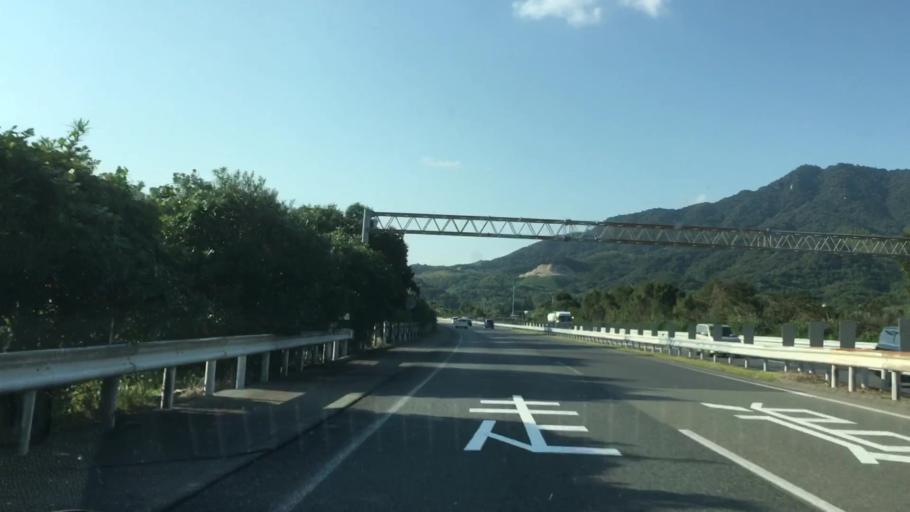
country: JP
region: Yamaguchi
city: Hofu
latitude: 34.0664
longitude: 131.6036
